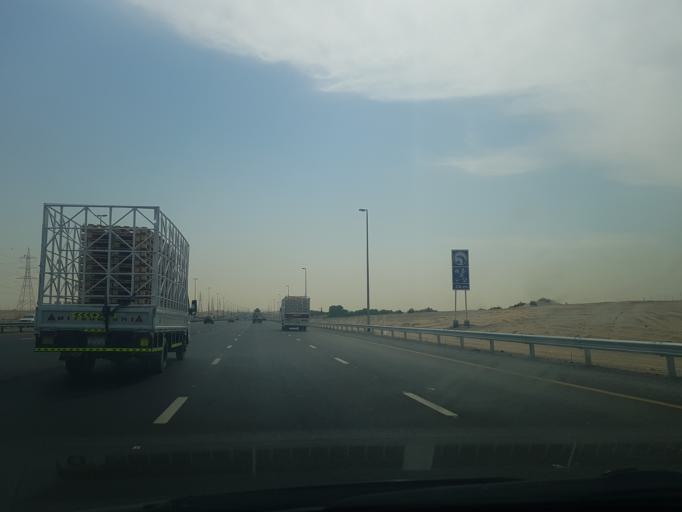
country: AE
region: Ash Shariqah
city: Sharjah
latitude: 25.2747
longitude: 55.5828
